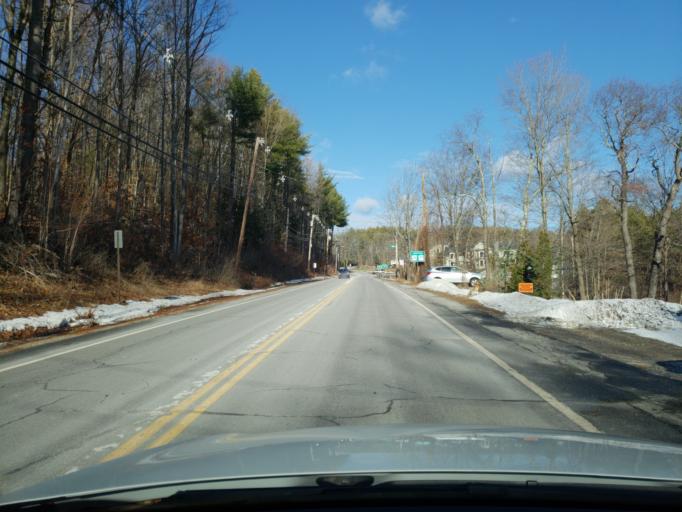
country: US
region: New Hampshire
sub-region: Hillsborough County
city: New Boston
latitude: 42.9794
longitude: -71.6927
